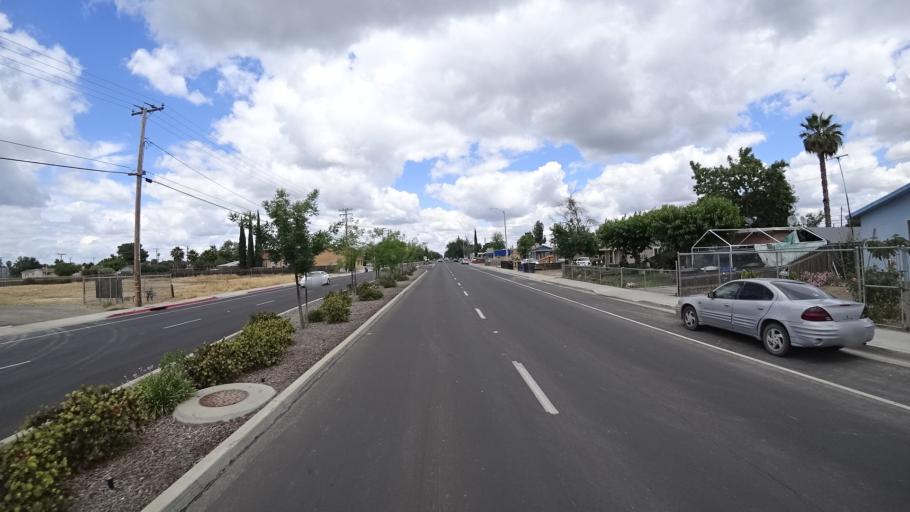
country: US
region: California
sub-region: Kings County
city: Hanford
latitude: 36.3450
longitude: -119.6370
